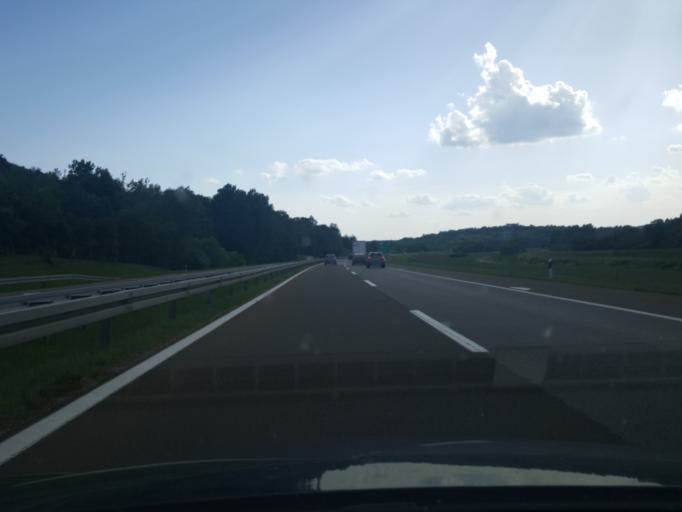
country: RS
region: Central Serbia
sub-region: Podunavski Okrug
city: Smederevo
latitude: 44.5745
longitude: 20.9253
